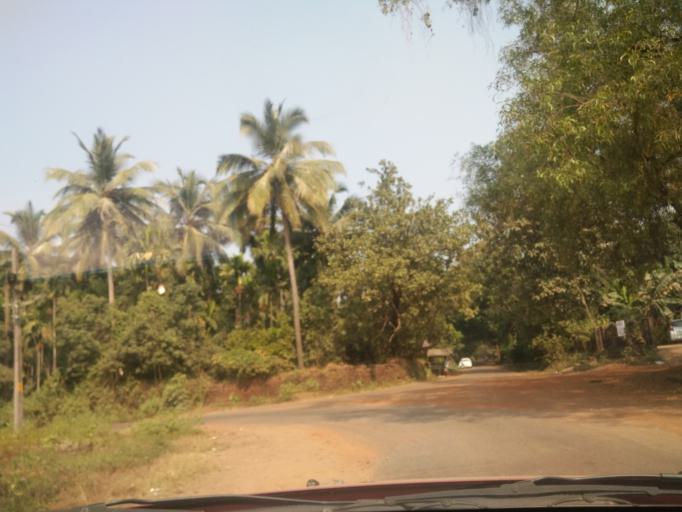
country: IN
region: Goa
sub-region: North Goa
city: Valpoy
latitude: 15.5036
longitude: 74.1399
